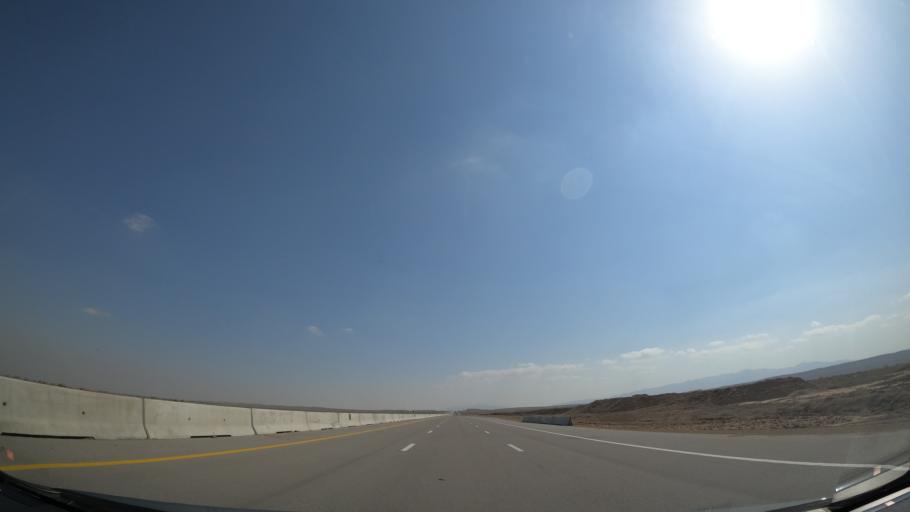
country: IR
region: Alborz
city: Nazarabad
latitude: 35.8194
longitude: 50.5155
